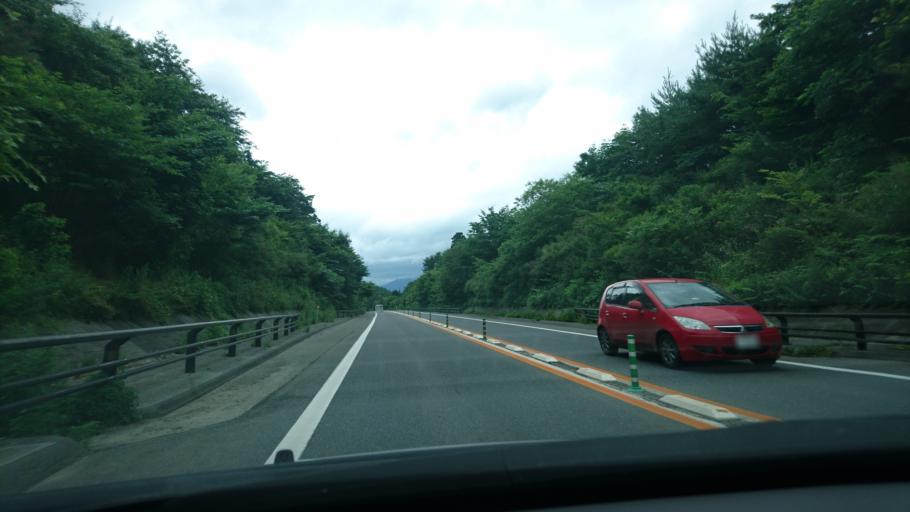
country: JP
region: Iwate
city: Ofunato
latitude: 39.0495
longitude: 141.7148
